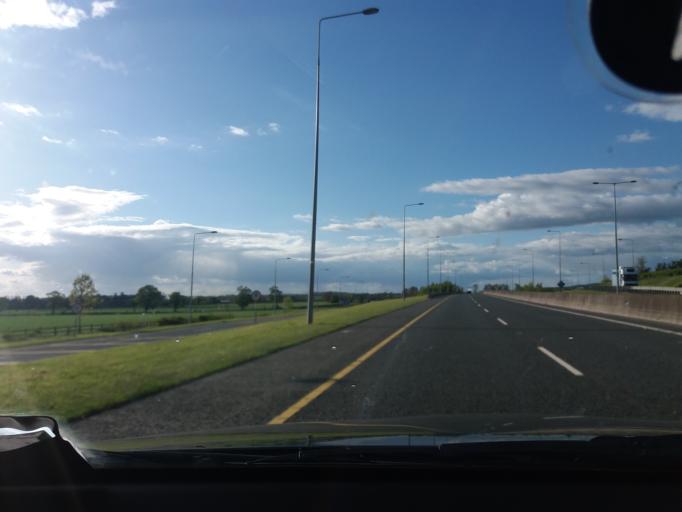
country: IE
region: Leinster
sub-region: Kildare
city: Castledermot
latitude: 52.8885
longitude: -6.8548
